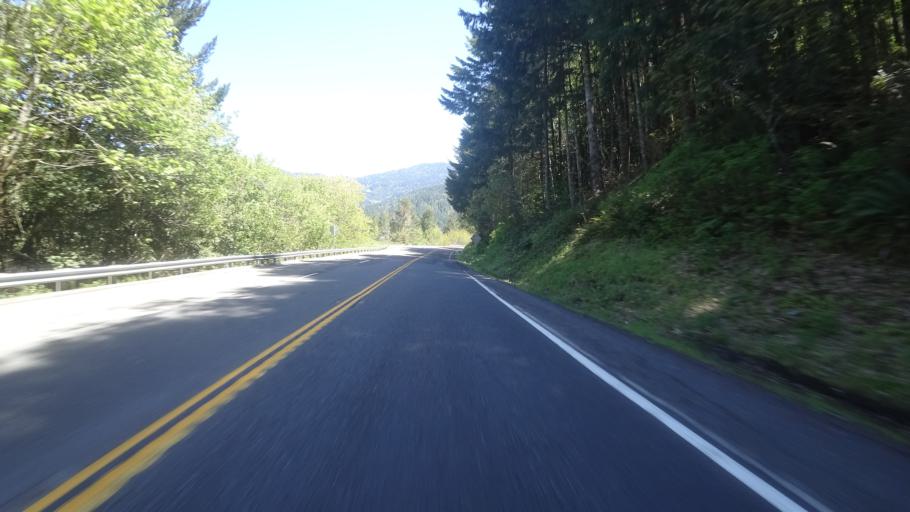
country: US
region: California
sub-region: Humboldt County
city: Blue Lake
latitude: 40.9049
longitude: -123.8249
